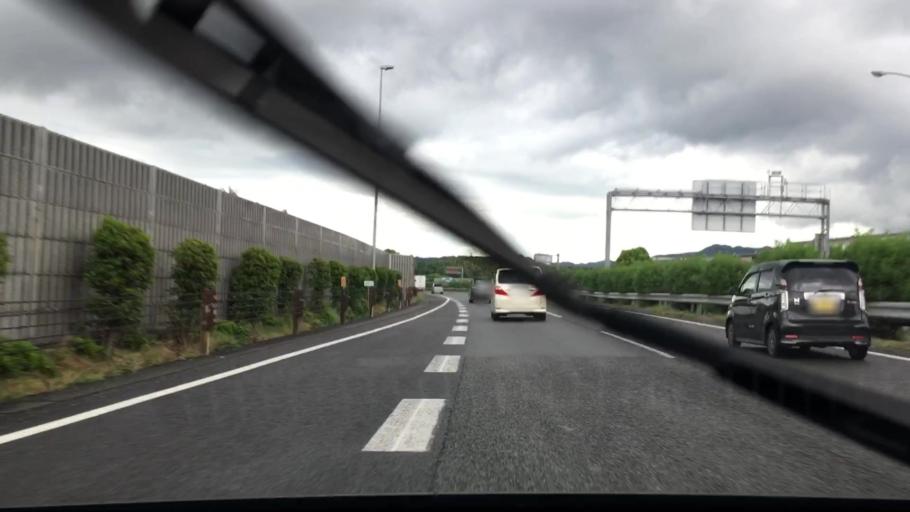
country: JP
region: Fukuoka
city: Sasaguri
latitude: 33.6330
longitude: 130.4906
